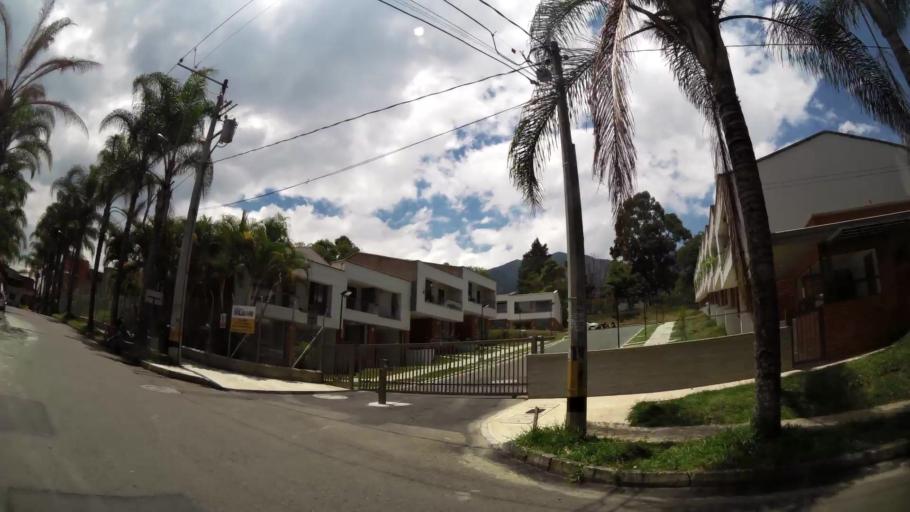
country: CO
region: Antioquia
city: La Estrella
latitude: 6.1614
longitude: -75.6401
